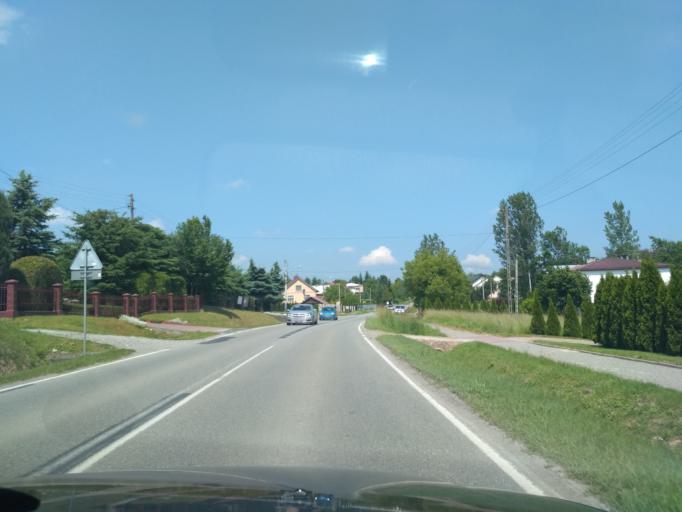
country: PL
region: Subcarpathian Voivodeship
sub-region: Powiat lancucki
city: Lancut
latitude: 50.0450
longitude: 22.2271
